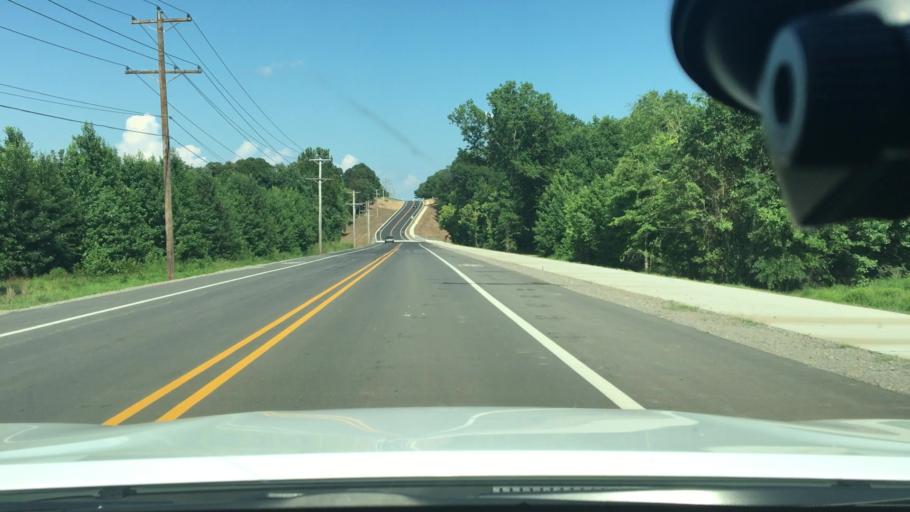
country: US
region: Arkansas
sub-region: Johnson County
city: Clarksville
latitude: 35.4620
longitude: -93.4999
